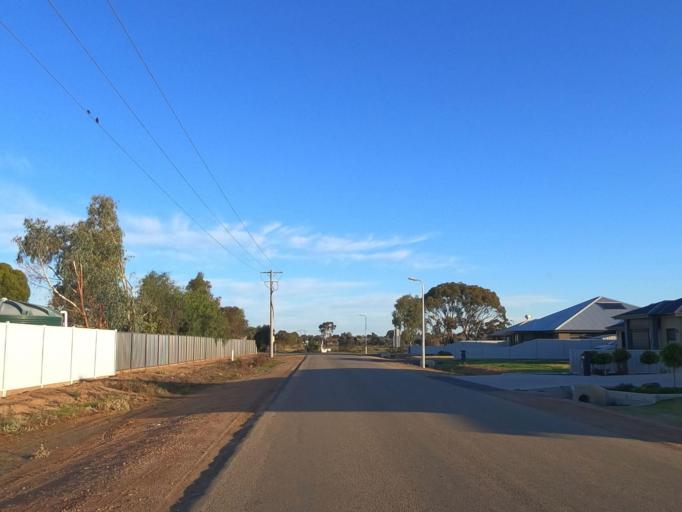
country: AU
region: Victoria
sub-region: Swan Hill
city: Swan Hill
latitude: -35.3320
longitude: 143.5343
